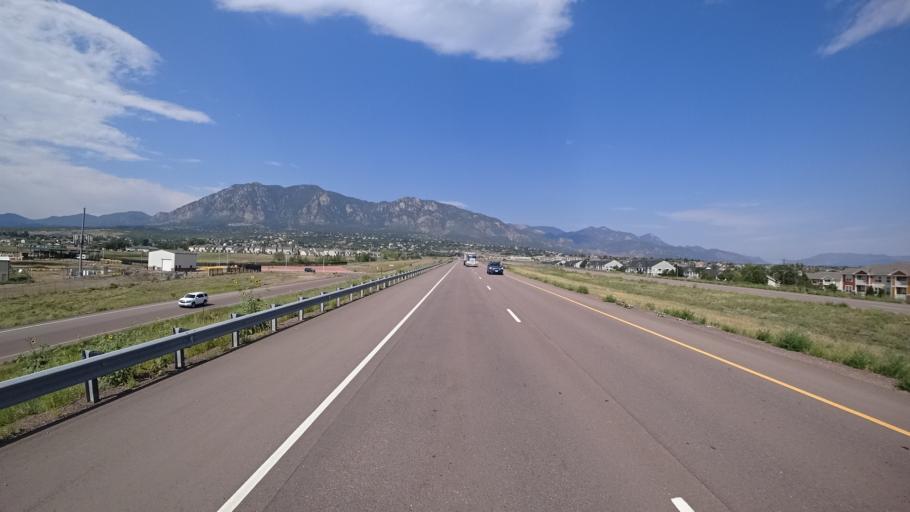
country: US
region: Colorado
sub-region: El Paso County
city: Stratmoor
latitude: 38.7657
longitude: -104.8022
